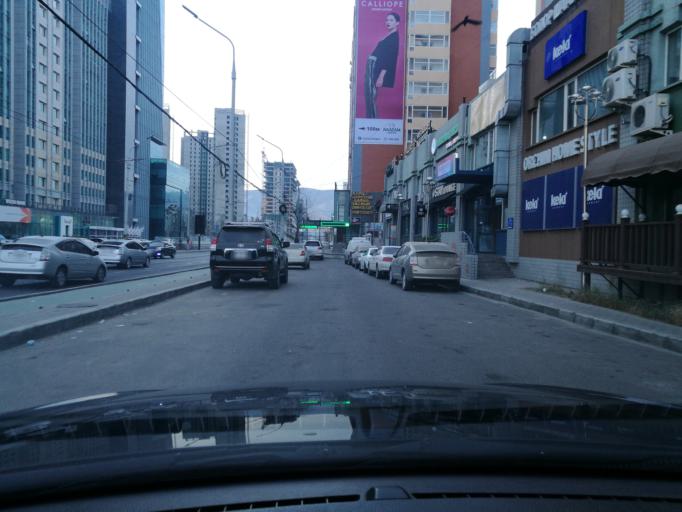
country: MN
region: Ulaanbaatar
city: Ulaanbaatar
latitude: 47.9052
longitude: 106.9117
